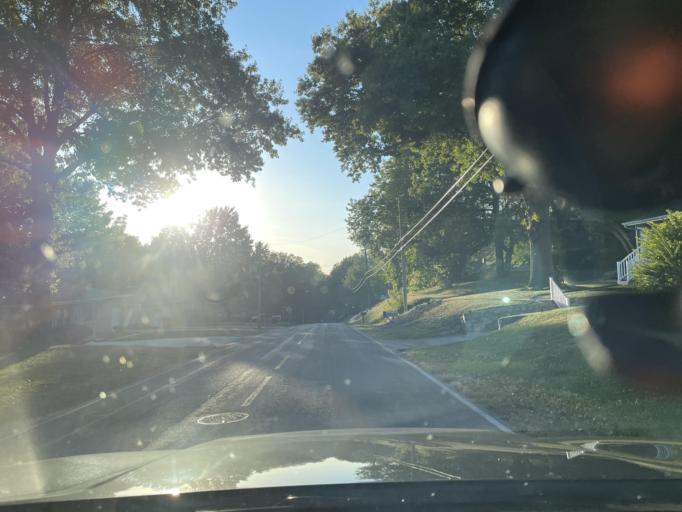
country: US
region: Missouri
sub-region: Andrew County
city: Country Club Village
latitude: 39.7994
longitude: -94.8251
